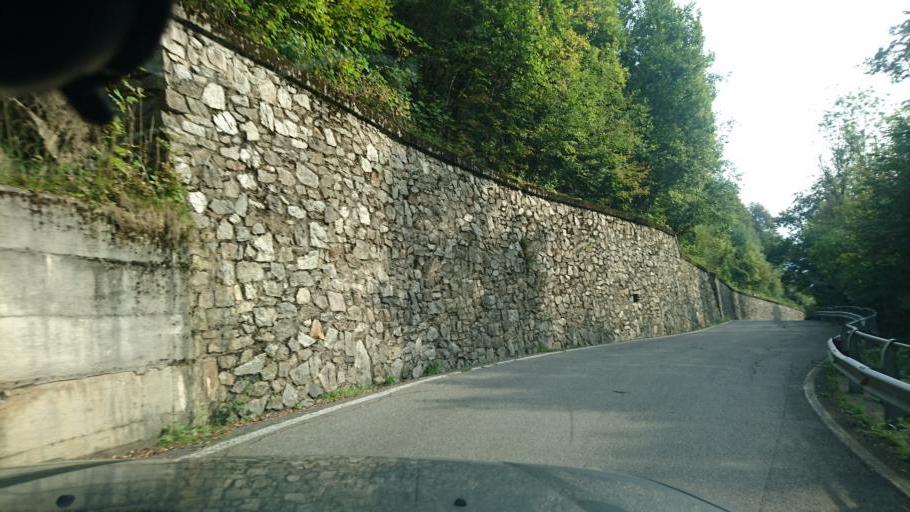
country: IT
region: Lombardy
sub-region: Provincia di Brescia
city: Paisco Loveno
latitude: 46.0753
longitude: 10.2785
